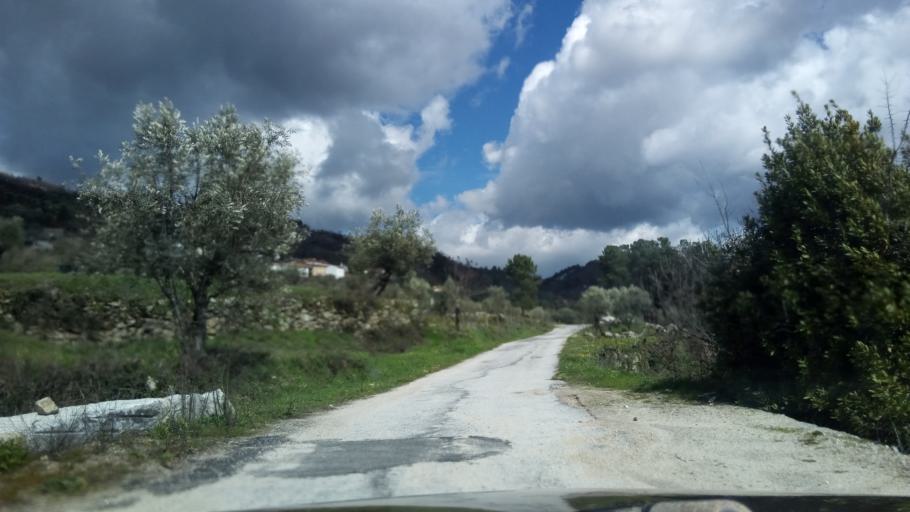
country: PT
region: Guarda
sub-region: Fornos de Algodres
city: Fornos de Algodres
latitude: 40.6591
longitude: -7.4957
